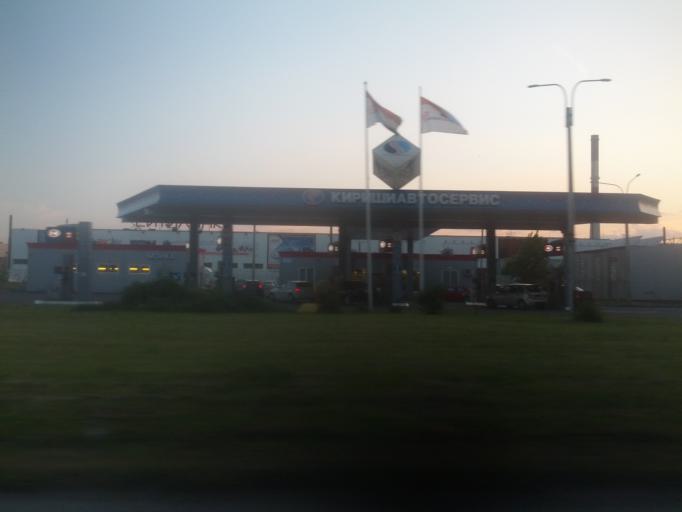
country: RU
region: St.-Petersburg
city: Staraya Derevnya
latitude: 59.9923
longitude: 30.2556
